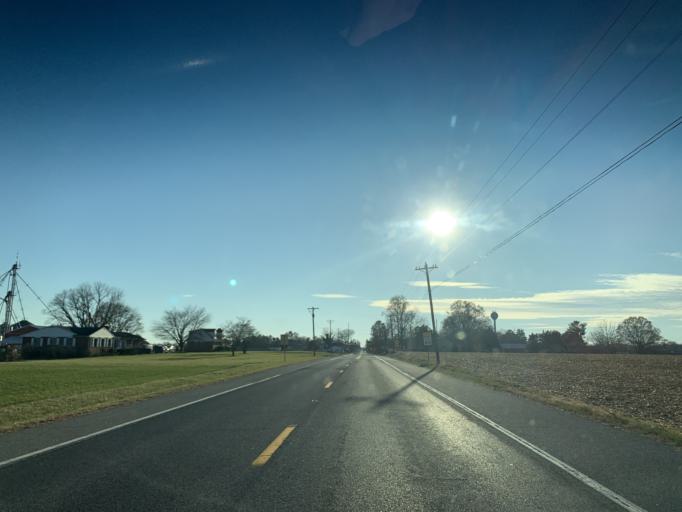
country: US
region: Maryland
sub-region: Queen Anne's County
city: Kingstown
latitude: 39.3102
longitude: -75.9903
